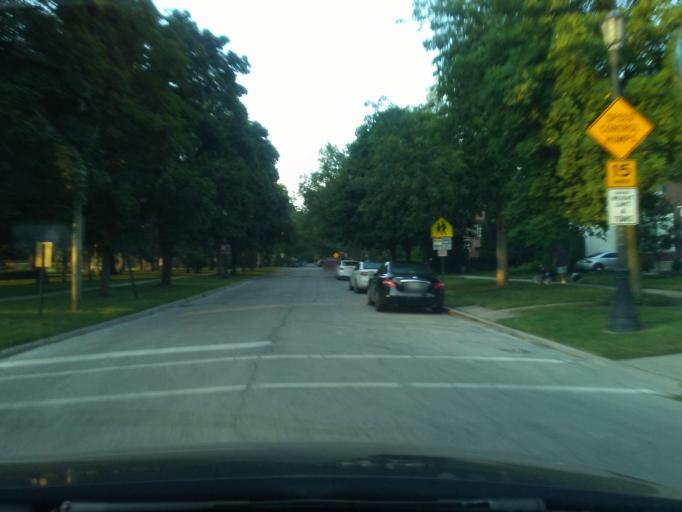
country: US
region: Illinois
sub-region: Cook County
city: Evanston
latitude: 42.0267
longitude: -87.6886
